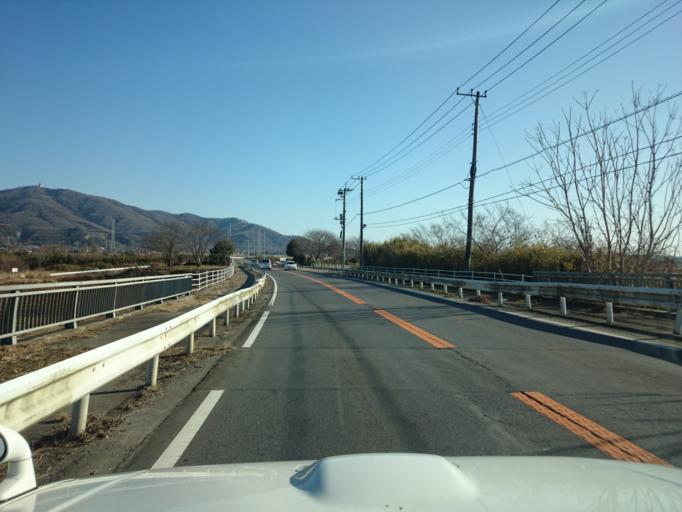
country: JP
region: Ibaraki
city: Tsukuba
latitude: 36.1435
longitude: 140.0924
